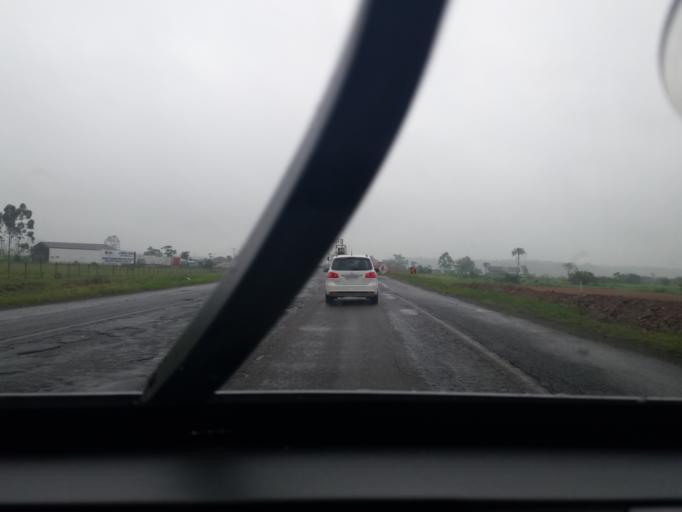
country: BR
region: Santa Catarina
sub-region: Navegantes
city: Navegantes
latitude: -26.8360
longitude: -48.7197
